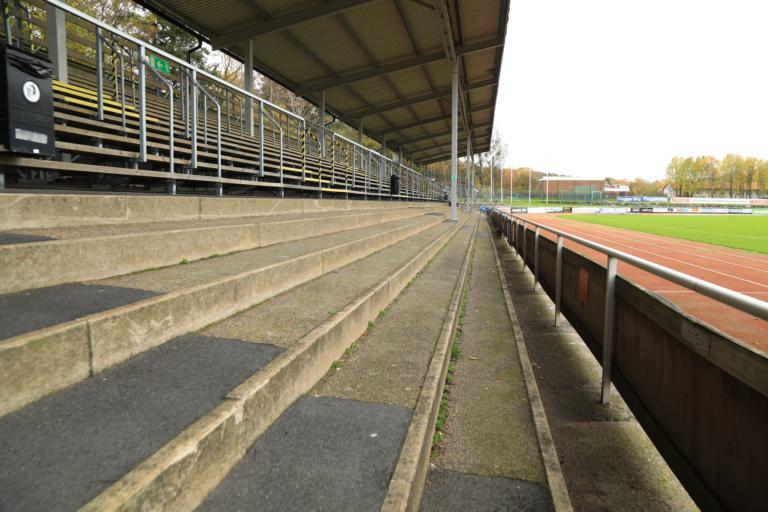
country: SE
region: Halland
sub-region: Varbergs Kommun
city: Varberg
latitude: 57.0987
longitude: 12.2661
